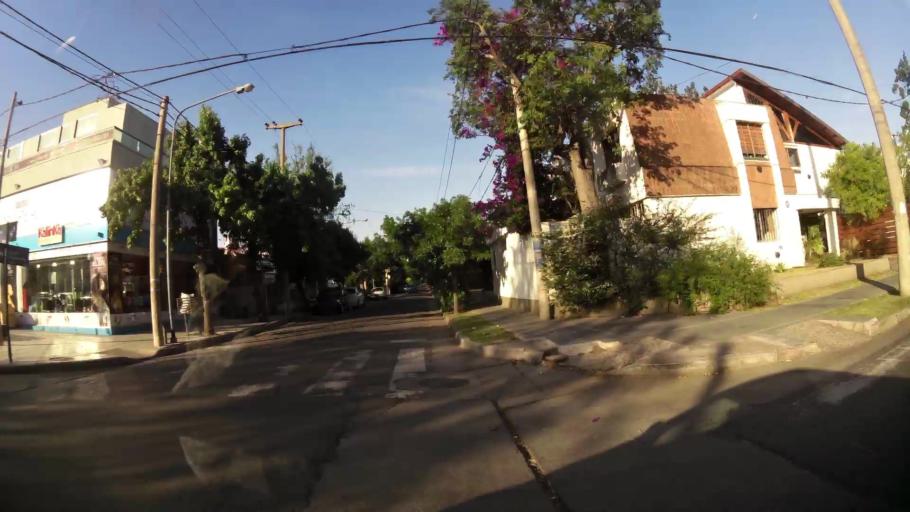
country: AR
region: Cordoba
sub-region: Departamento de Capital
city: Cordoba
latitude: -31.3836
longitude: -64.2355
